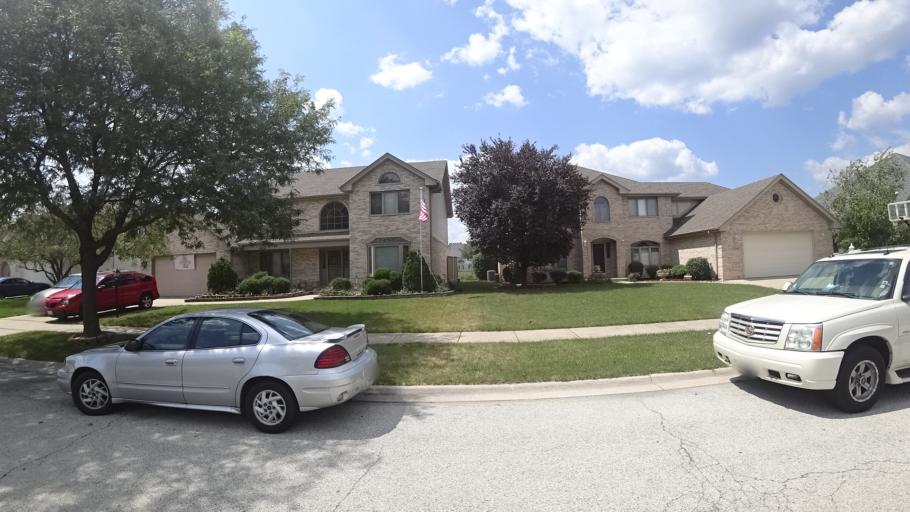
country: US
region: Illinois
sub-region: Cook County
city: Oak Forest
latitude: 41.6178
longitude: -87.7718
